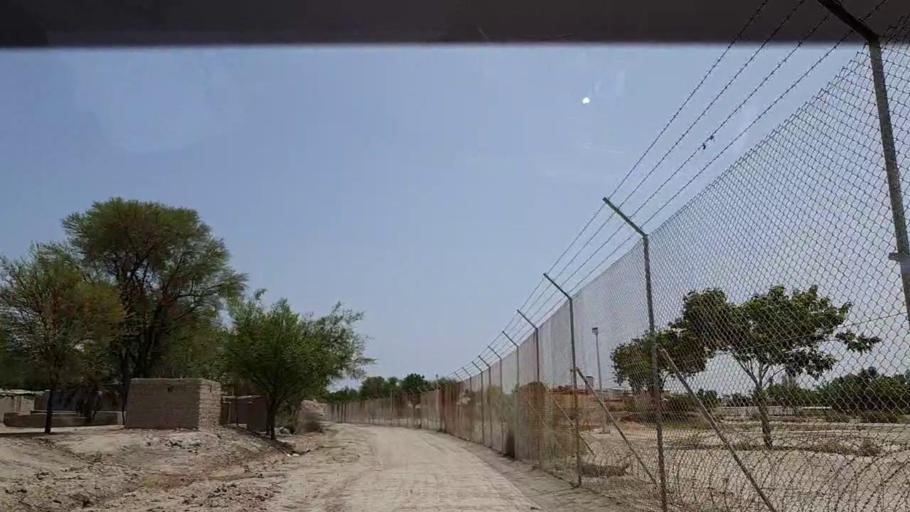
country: PK
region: Sindh
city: Johi
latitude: 26.7102
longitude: 67.6677
